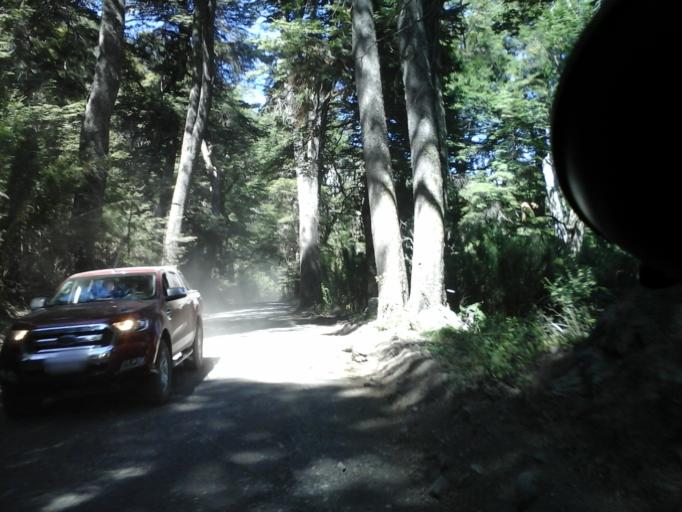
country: AR
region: Neuquen
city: Villa La Angostura
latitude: -41.2117
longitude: -71.8077
